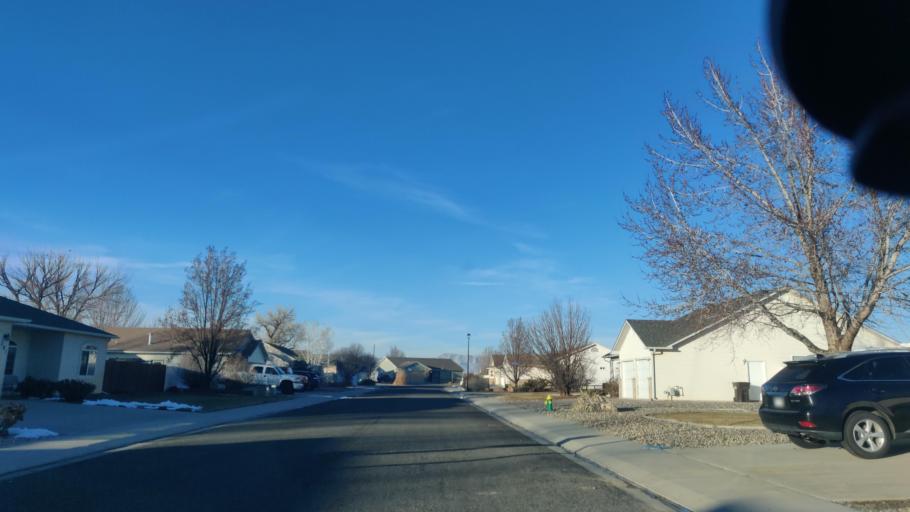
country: US
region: Colorado
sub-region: Mesa County
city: Grand Junction
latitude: 39.0611
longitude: -108.5241
